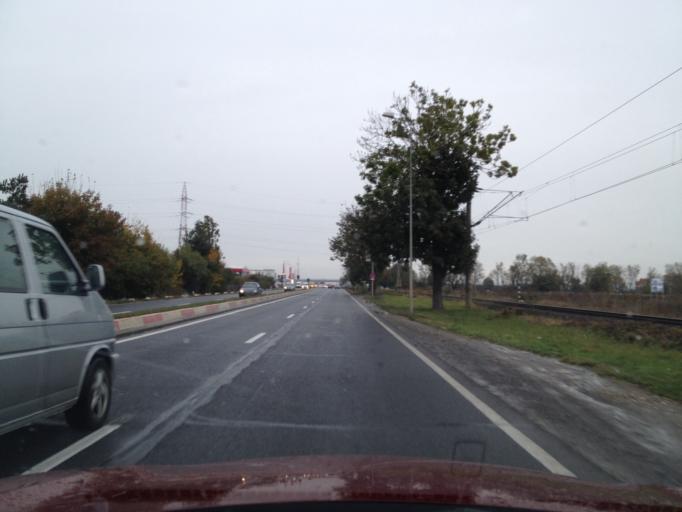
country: RO
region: Brasov
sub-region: Comuna Sanpetru
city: Sanpetru
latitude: 45.6788
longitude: 25.6536
